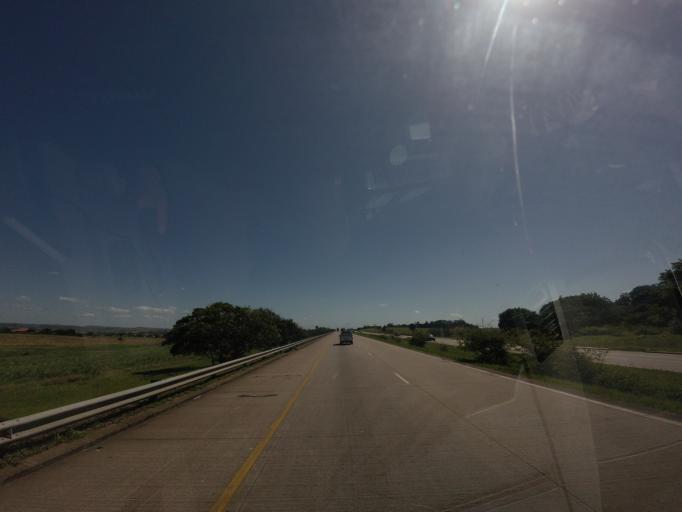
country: ZA
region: KwaZulu-Natal
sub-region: iLembe District Municipality
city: Stanger
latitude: -29.4140
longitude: 31.2783
